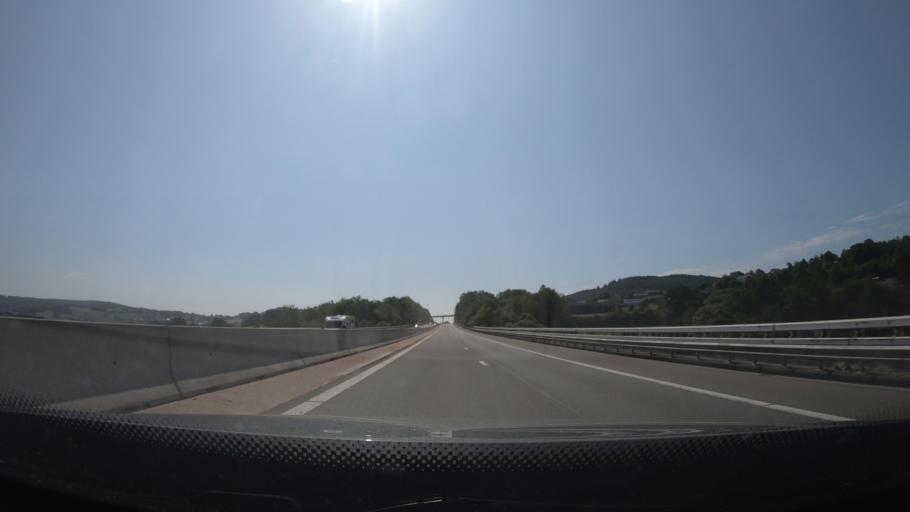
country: BE
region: Wallonia
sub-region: Province de Liege
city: Malmedy
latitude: 50.3864
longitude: 5.9934
